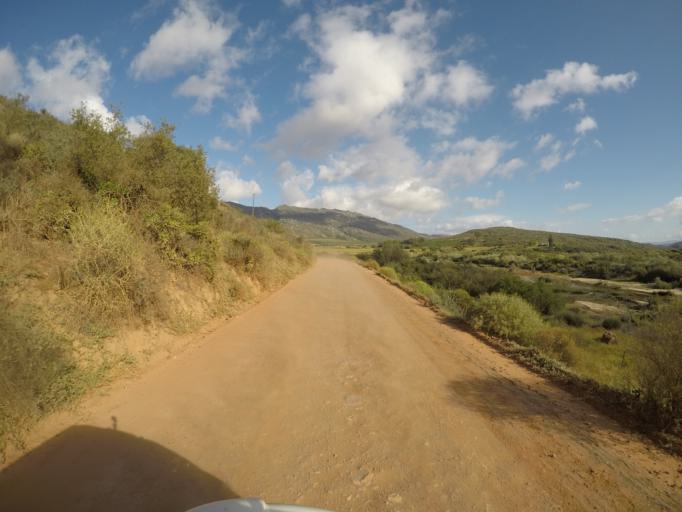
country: ZA
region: Western Cape
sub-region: West Coast District Municipality
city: Clanwilliam
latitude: -32.3638
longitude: 18.9461
